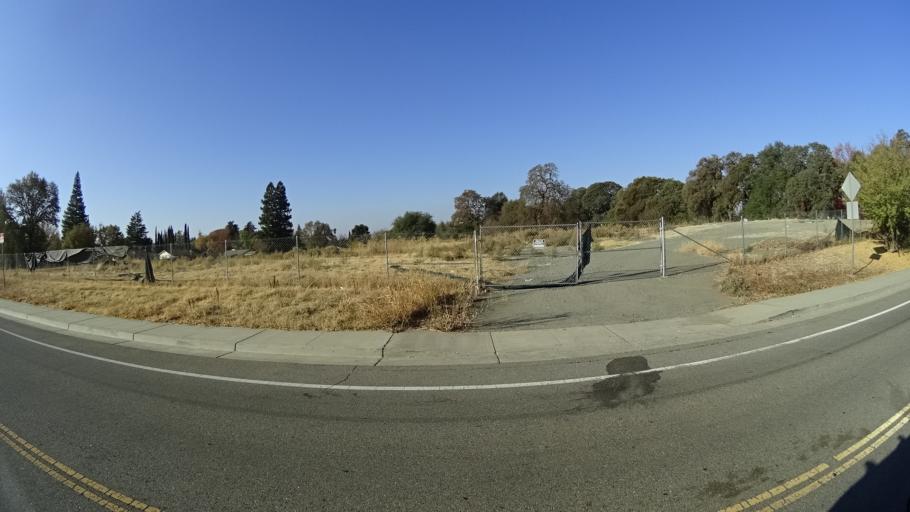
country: US
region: California
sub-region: Sacramento County
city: Citrus Heights
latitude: 38.7109
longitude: -121.2538
